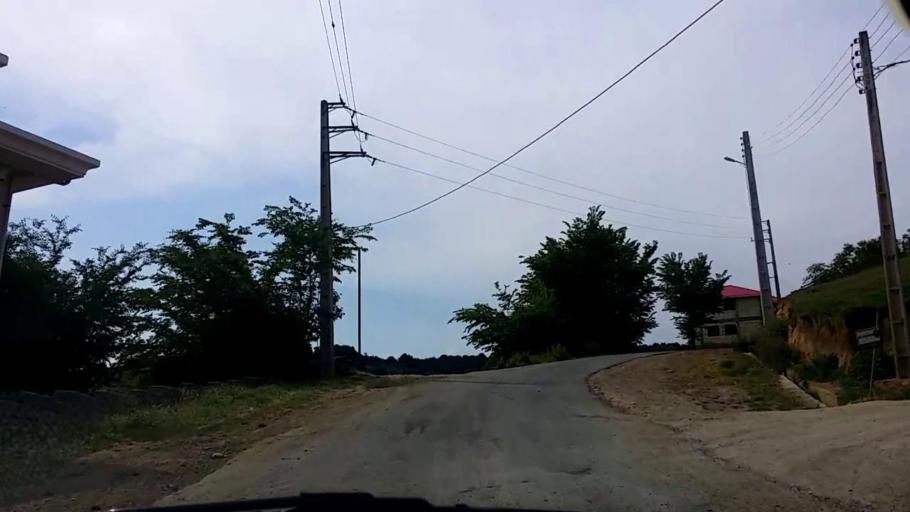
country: IR
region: Mazandaran
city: `Abbasabad
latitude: 36.5519
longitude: 51.1825
